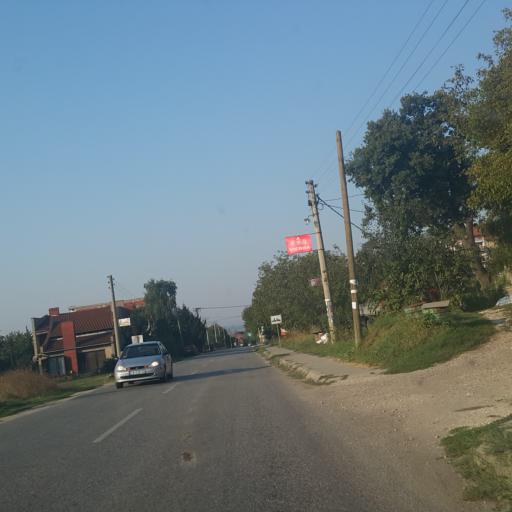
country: RS
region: Central Serbia
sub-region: Zajecarski Okrug
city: Zajecar
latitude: 43.9170
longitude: 22.2874
